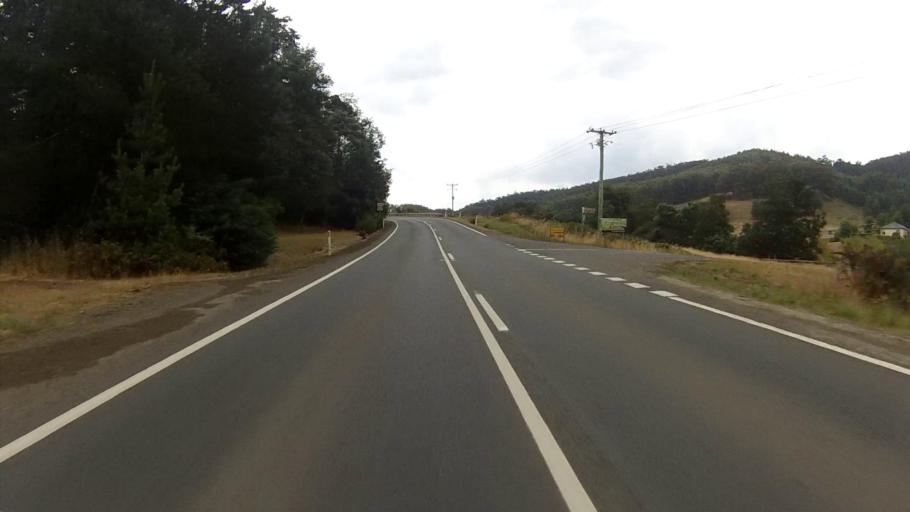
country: AU
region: Tasmania
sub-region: Huon Valley
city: Cygnet
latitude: -43.1360
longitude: 147.0543
